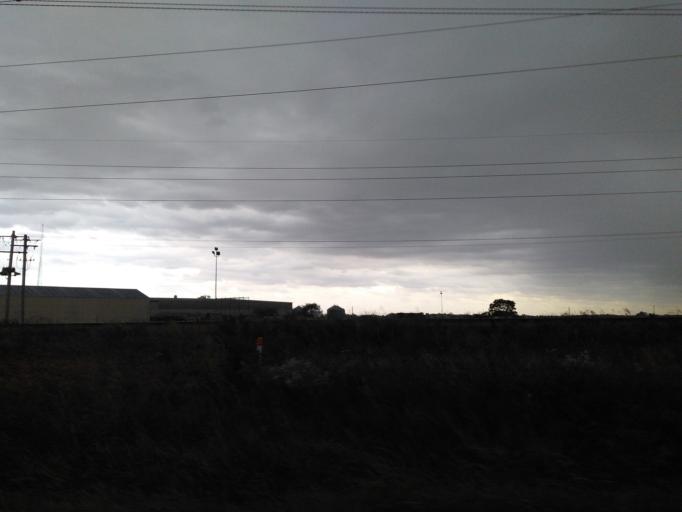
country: US
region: Illinois
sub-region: Madison County
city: Highland
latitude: 38.7386
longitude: -89.6998
